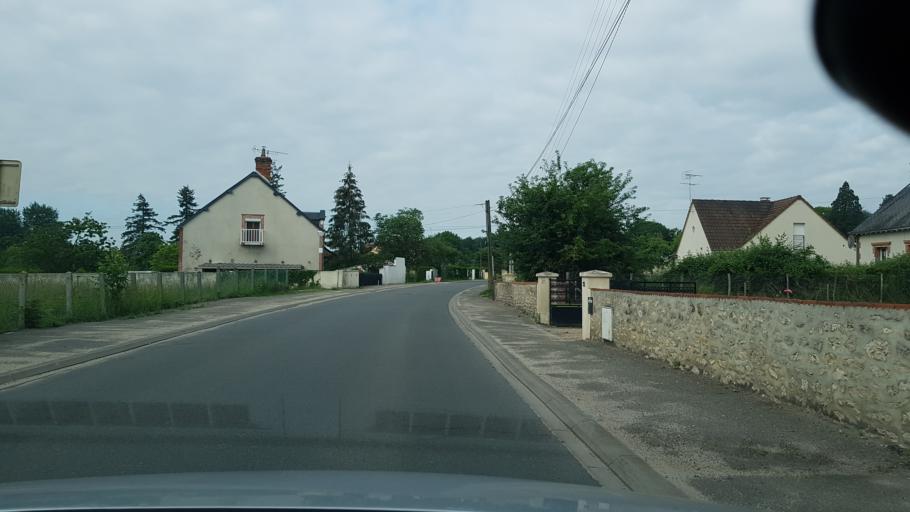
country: FR
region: Centre
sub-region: Departement du Loir-et-Cher
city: Romorantin-Lanthenay
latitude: 47.3524
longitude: 1.7277
